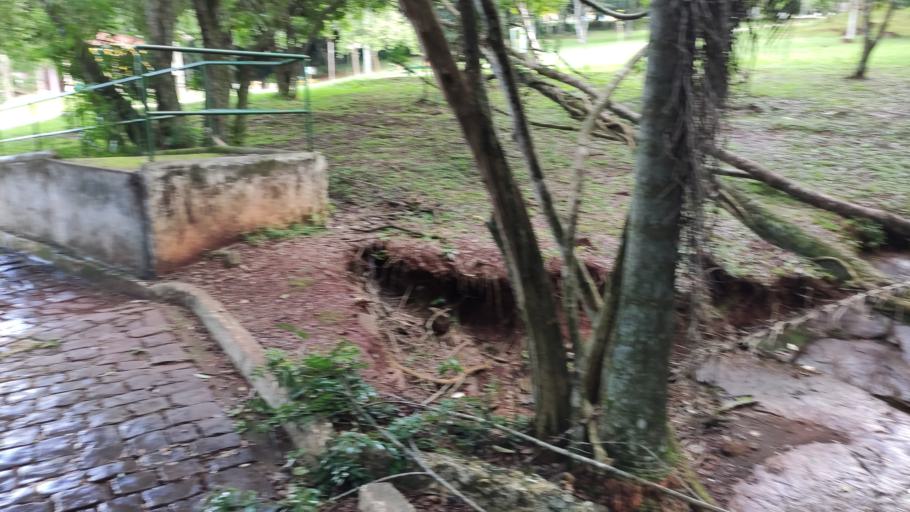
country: BR
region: Parana
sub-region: Londrina
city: Londrina
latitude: -23.3444
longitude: -51.1412
